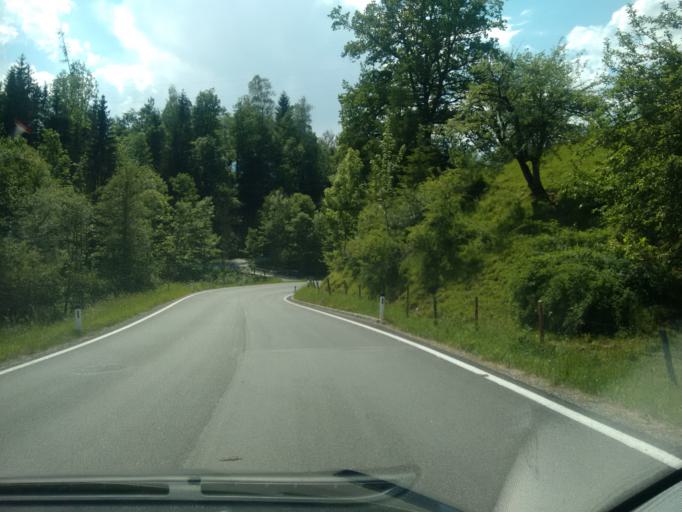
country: AT
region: Upper Austria
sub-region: Politischer Bezirk Kirchdorf an der Krems
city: Rossleithen
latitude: 47.7107
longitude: 14.2160
